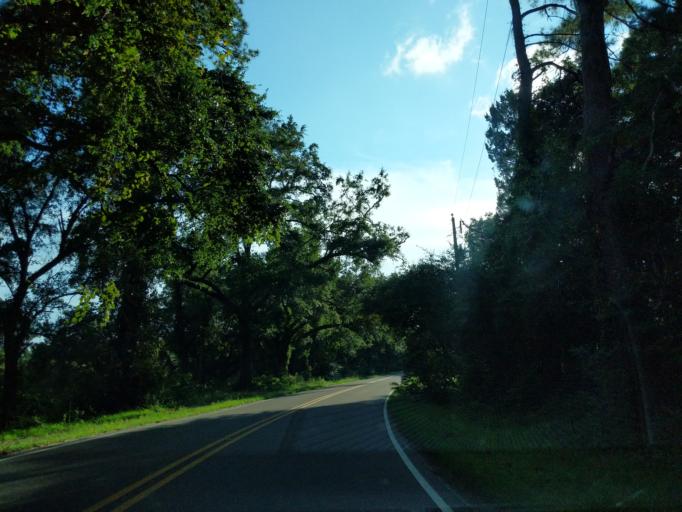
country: US
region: South Carolina
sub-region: Charleston County
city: Awendaw
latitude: 33.0926
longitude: -79.4710
